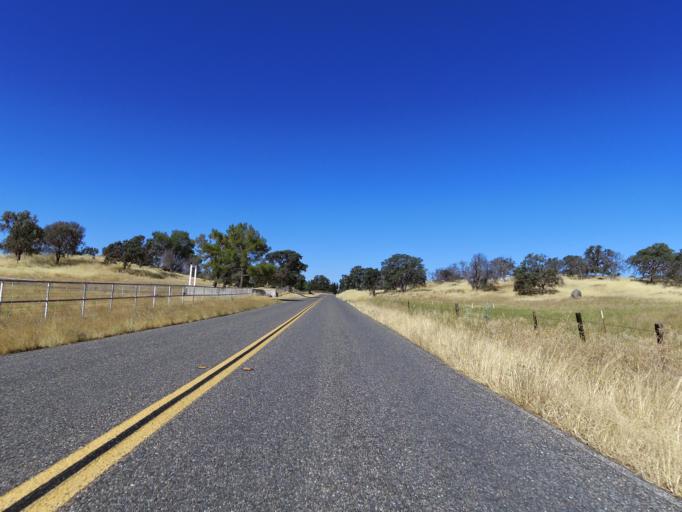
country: US
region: California
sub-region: Mariposa County
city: Mariposa
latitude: 37.4757
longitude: -120.1195
